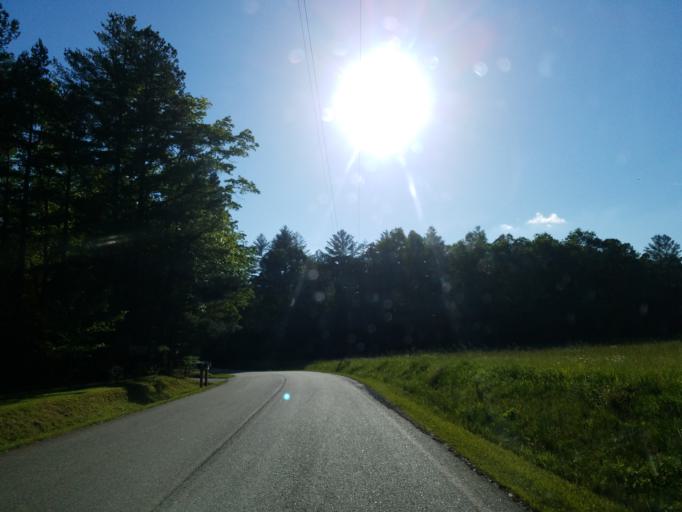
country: US
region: Georgia
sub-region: Fannin County
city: Blue Ridge
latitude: 34.7451
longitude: -84.1452
